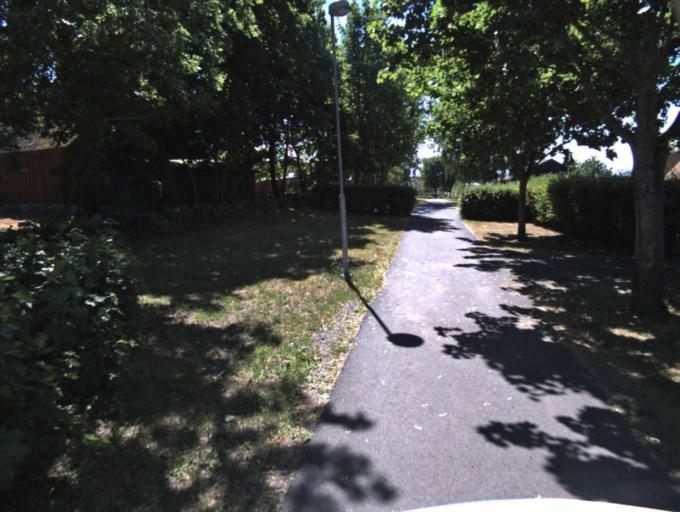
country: SE
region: Skane
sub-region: Kristianstads Kommun
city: Onnestad
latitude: 56.0576
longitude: 14.0211
